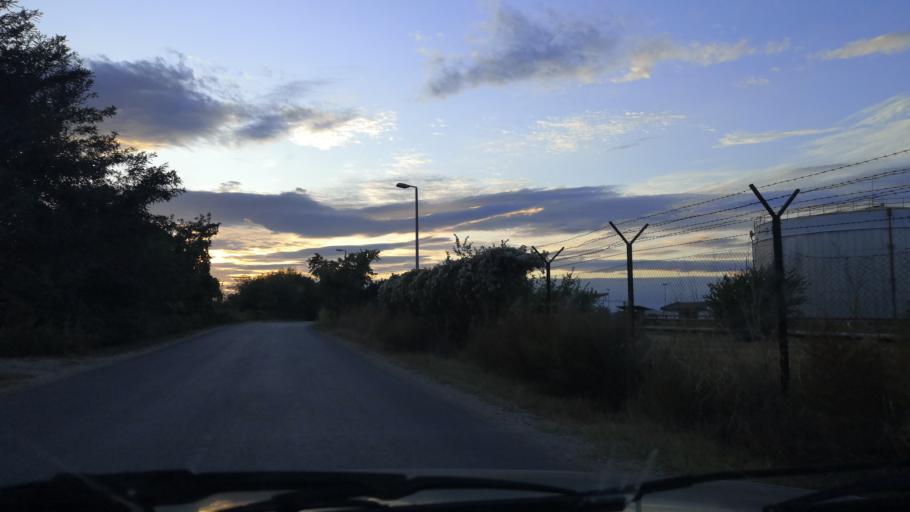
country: RO
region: Mehedinti
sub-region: Comuna Gruia
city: Izvoarele
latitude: 44.2867
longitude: 22.6275
